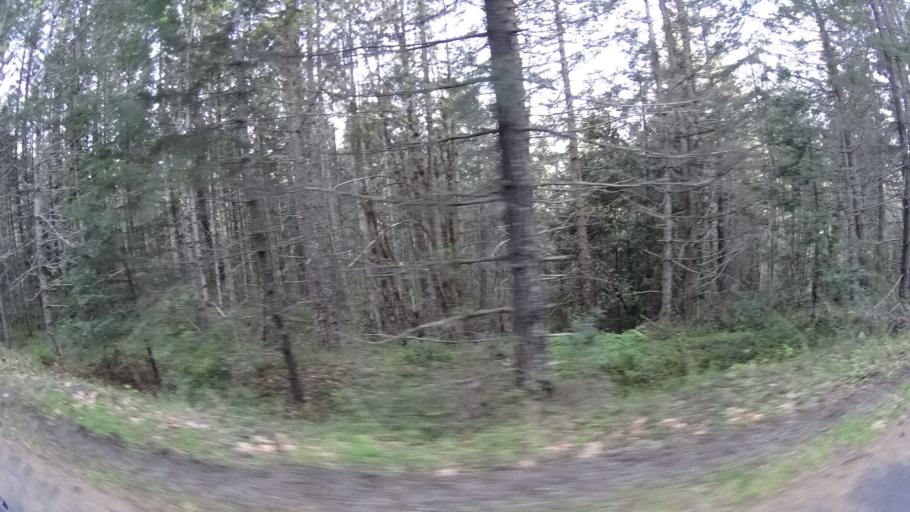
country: US
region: California
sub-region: Humboldt County
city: Bayside
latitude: 40.6805
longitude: -123.9378
